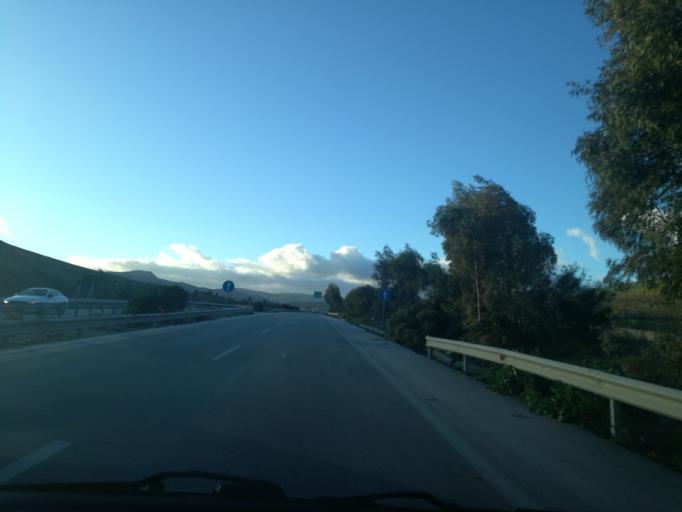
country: IT
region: Sicily
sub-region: Palermo
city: Castellana Sicula
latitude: 37.7409
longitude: 13.9997
